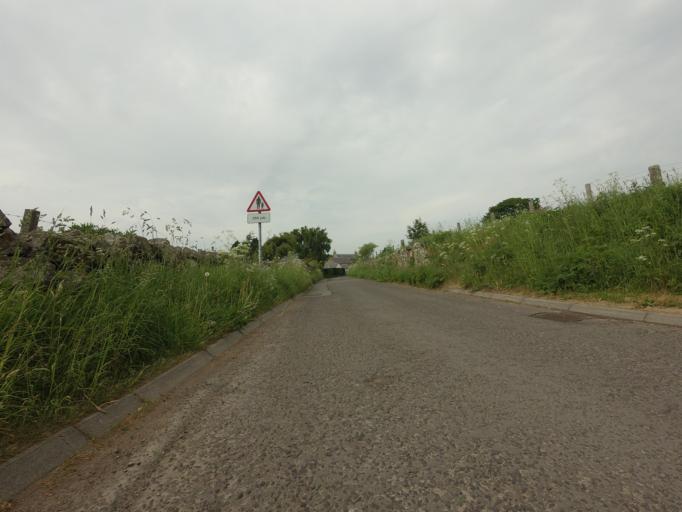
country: GB
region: Scotland
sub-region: Fife
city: Ballingry
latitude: 56.2218
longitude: -3.3460
